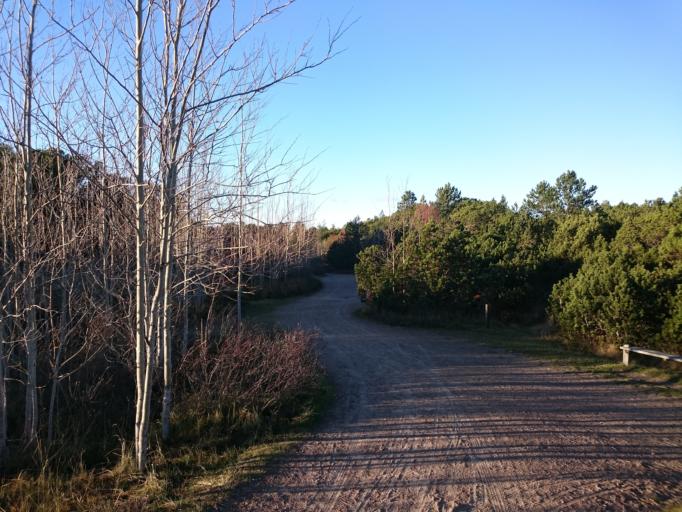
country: DK
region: North Denmark
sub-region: Frederikshavn Kommune
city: Skagen
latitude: 57.7144
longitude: 10.5479
